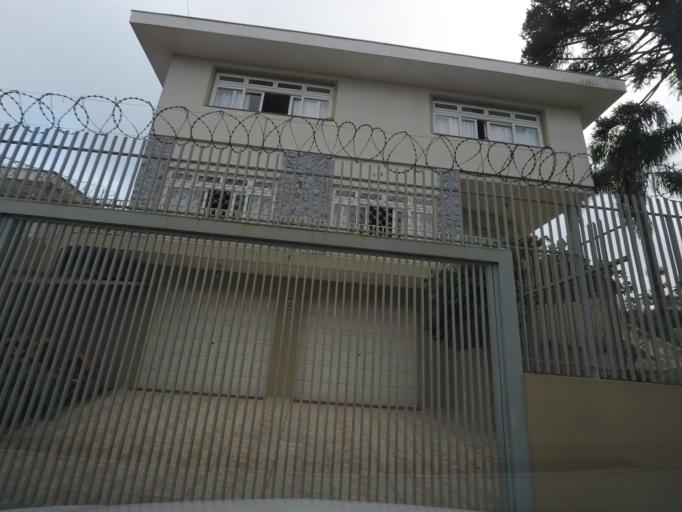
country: BR
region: Parana
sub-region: Curitiba
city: Curitiba
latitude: -25.4438
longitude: -49.2457
